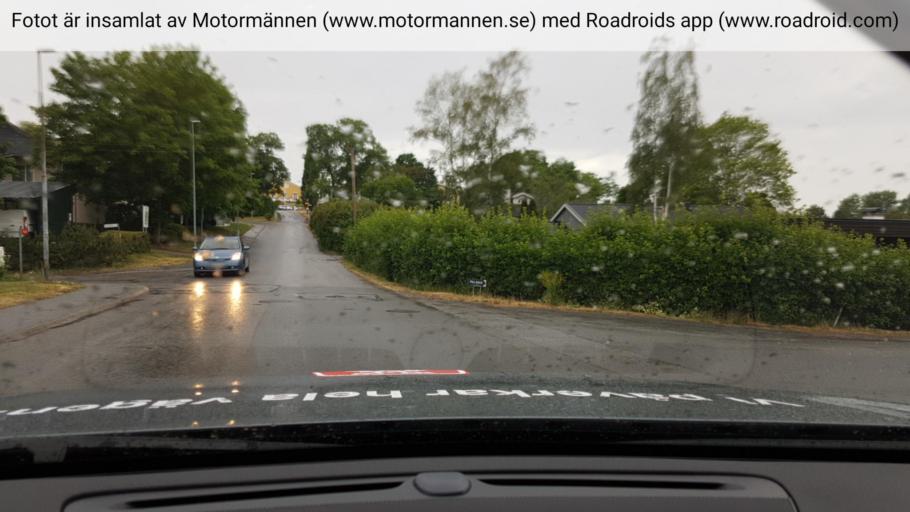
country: SE
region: Stockholm
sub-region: Vallentuna Kommun
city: Vallentuna
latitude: 59.5184
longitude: 18.0655
